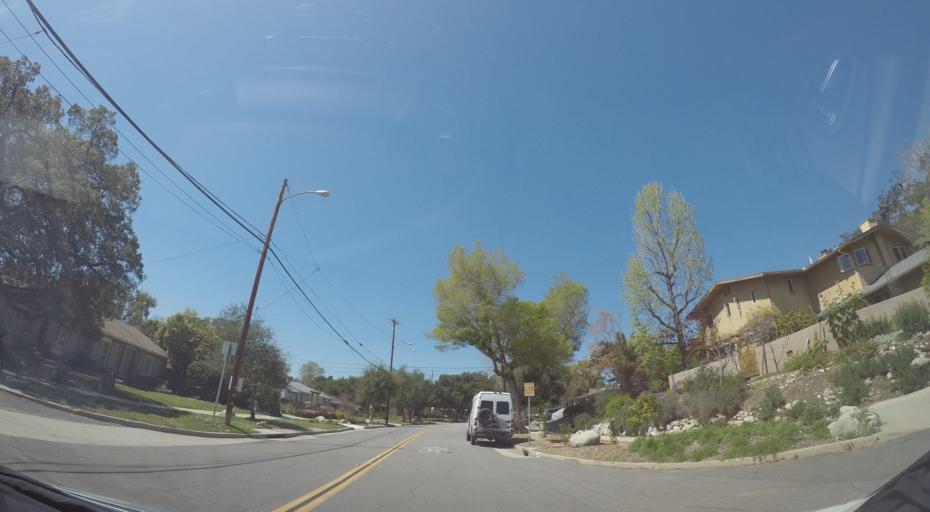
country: US
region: California
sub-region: Los Angeles County
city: Altadena
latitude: 34.1809
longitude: -118.1024
